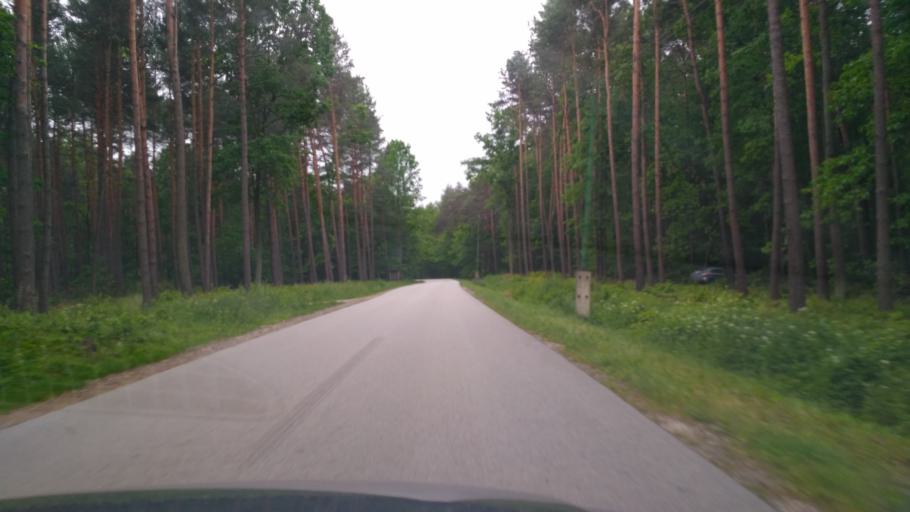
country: PL
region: Subcarpathian Voivodeship
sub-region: Powiat ropczycko-sedziszowski
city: Sedziszow Malopolski
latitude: 50.1282
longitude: 21.6715
